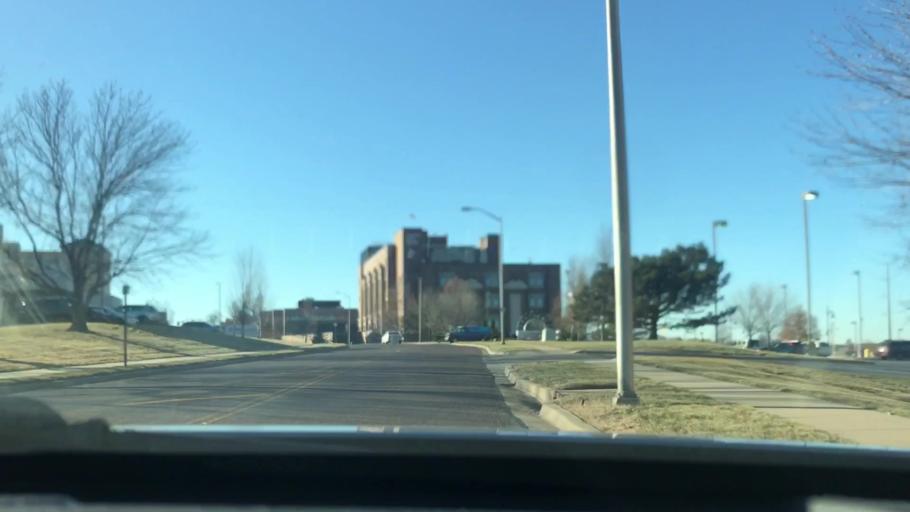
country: US
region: Kansas
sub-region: Johnson County
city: Leawood
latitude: 38.9295
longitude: -94.6501
